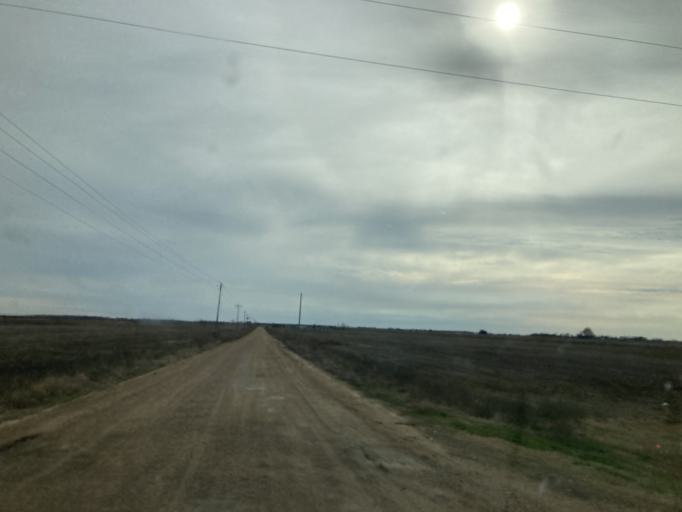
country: US
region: Mississippi
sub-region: Humphreys County
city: Belzoni
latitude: 33.1832
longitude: -90.5722
